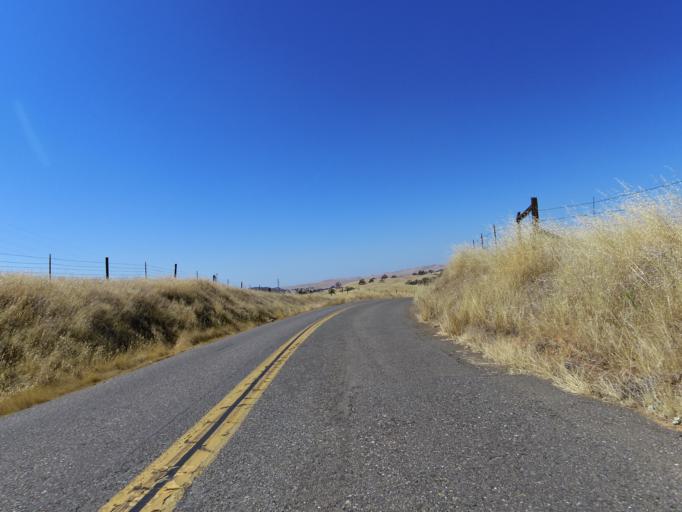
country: US
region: California
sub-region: Merced County
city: Planada
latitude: 37.5480
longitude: -120.3262
